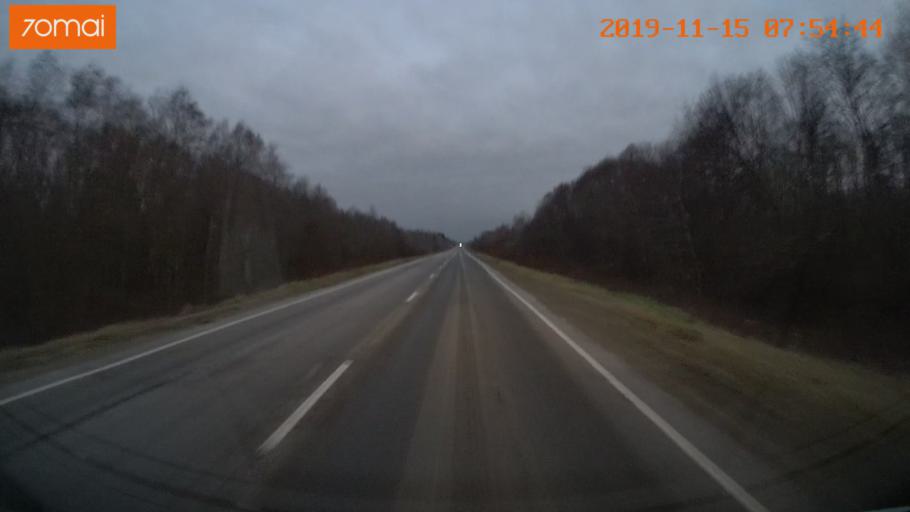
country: RU
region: Vologda
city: Cherepovets
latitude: 58.9016
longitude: 38.1723
